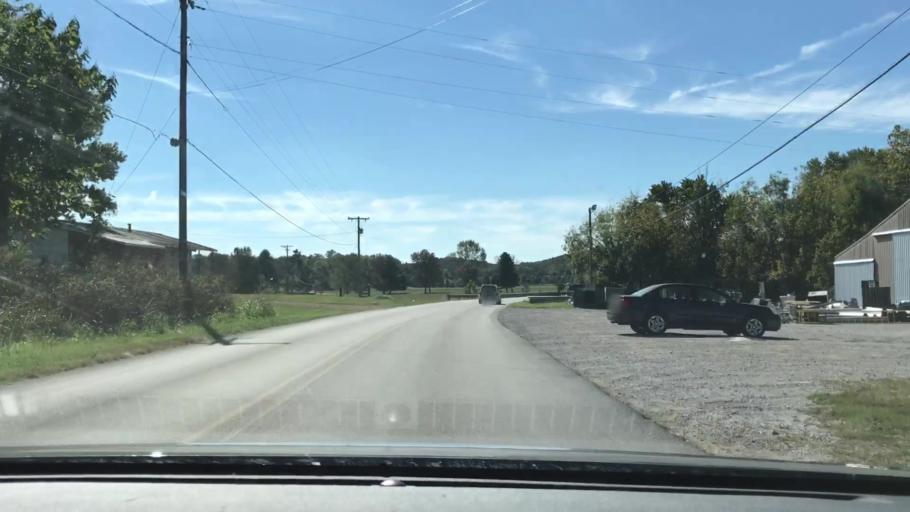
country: US
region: Kentucky
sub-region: Logan County
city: Russellville
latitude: 36.8413
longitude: -86.8705
